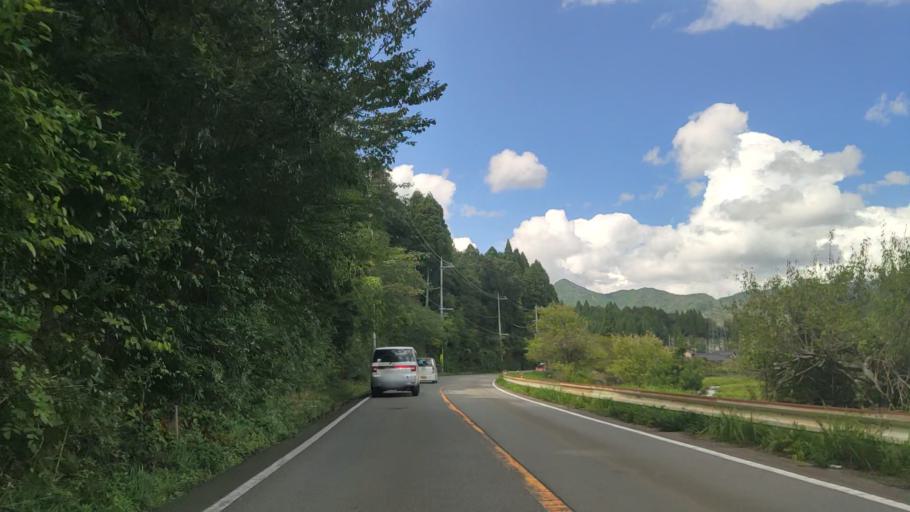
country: JP
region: Hyogo
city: Toyooka
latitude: 35.4762
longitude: 134.9519
